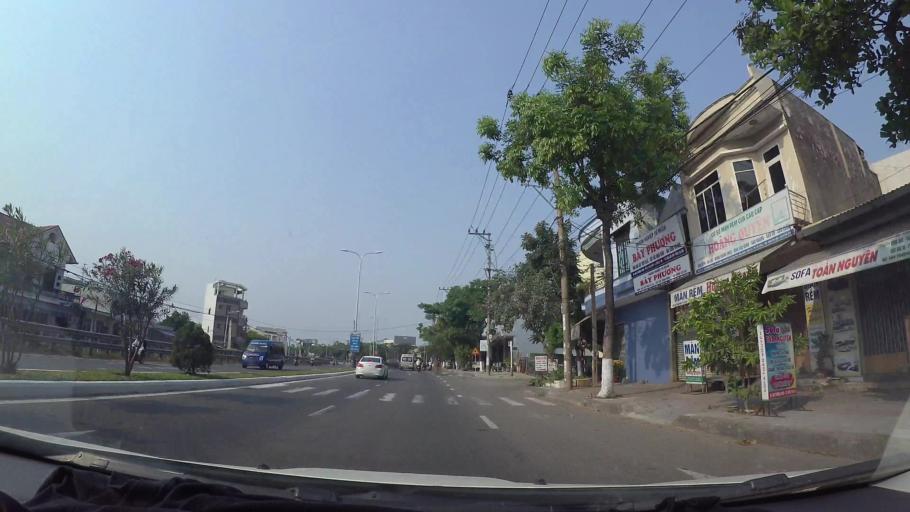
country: VN
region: Da Nang
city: Cam Le
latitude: 16.0189
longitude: 108.1939
